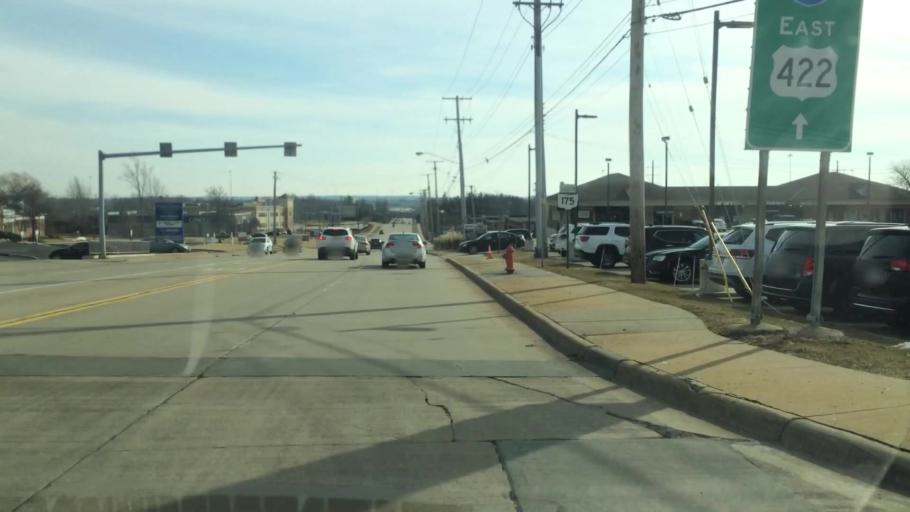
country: US
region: Ohio
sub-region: Cuyahoga County
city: Orange
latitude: 41.4350
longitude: -81.4980
